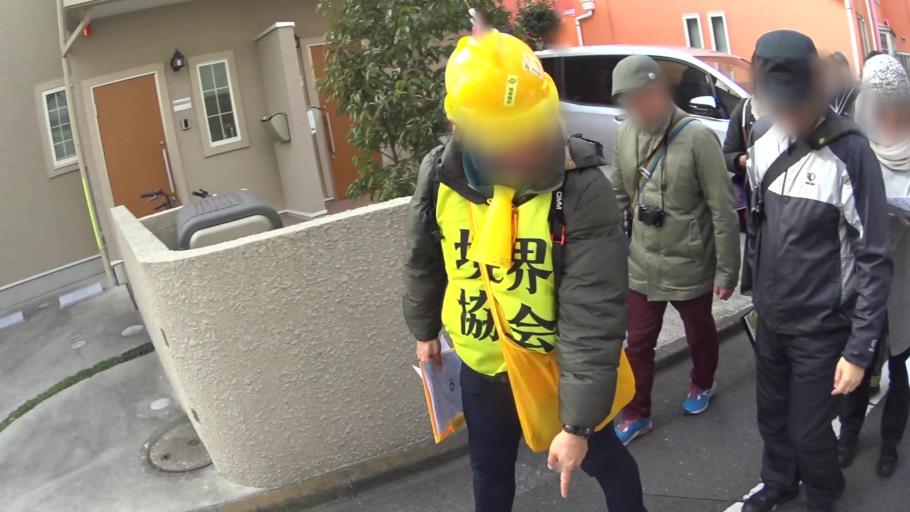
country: JP
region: Tokyo
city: Mitaka-shi
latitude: 35.6922
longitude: 139.5903
